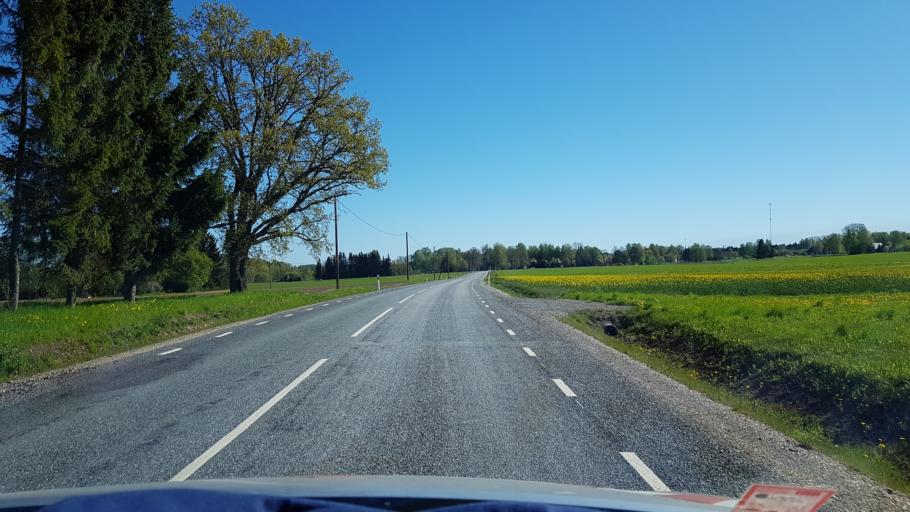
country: EE
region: Polvamaa
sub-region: Polva linn
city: Polva
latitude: 58.1519
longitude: 27.1758
